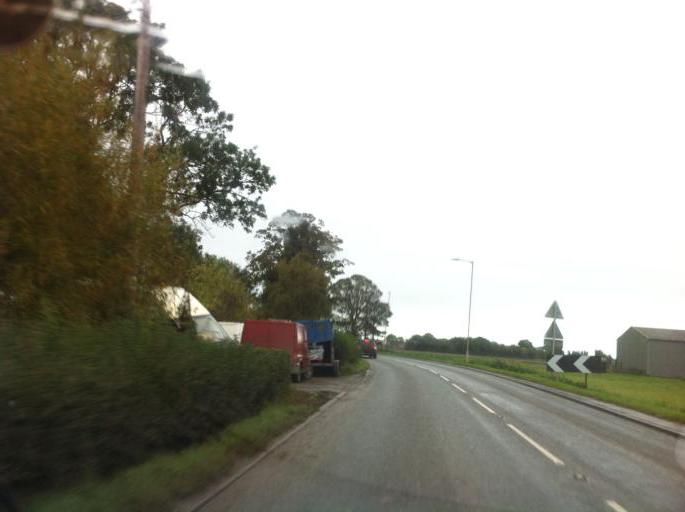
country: GB
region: England
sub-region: Lincolnshire
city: Wainfleet All Saints
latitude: 53.0321
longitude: 0.1148
